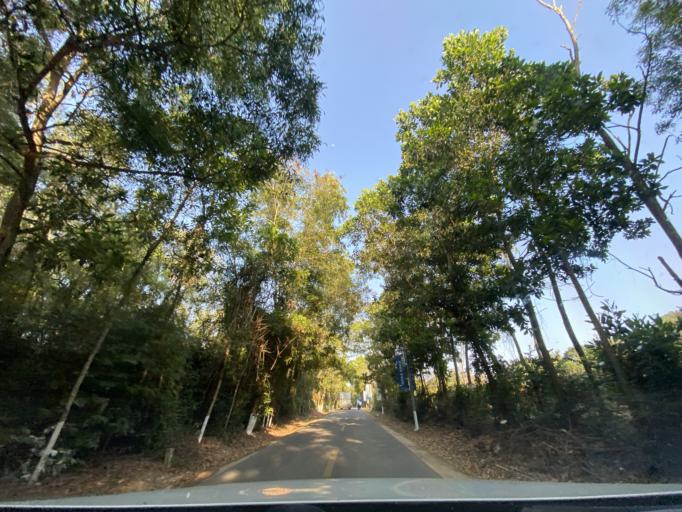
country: CN
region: Hainan
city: Yingzhou
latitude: 18.3878
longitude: 109.8248
